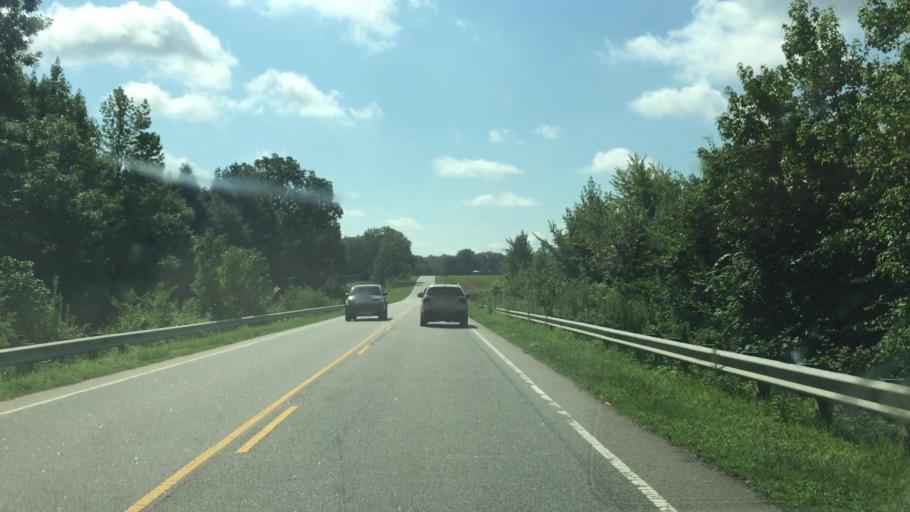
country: US
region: North Carolina
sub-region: Anson County
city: Polkton
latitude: 35.0252
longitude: -80.2299
